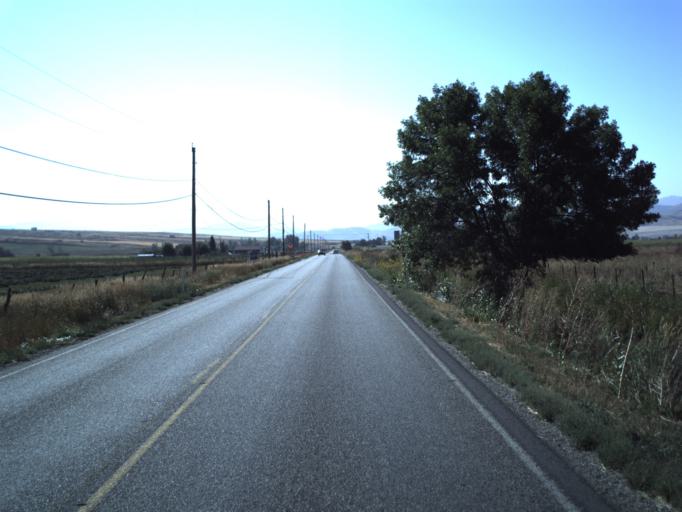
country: US
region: Utah
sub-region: Cache County
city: Hyrum
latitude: 41.6176
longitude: -111.8327
